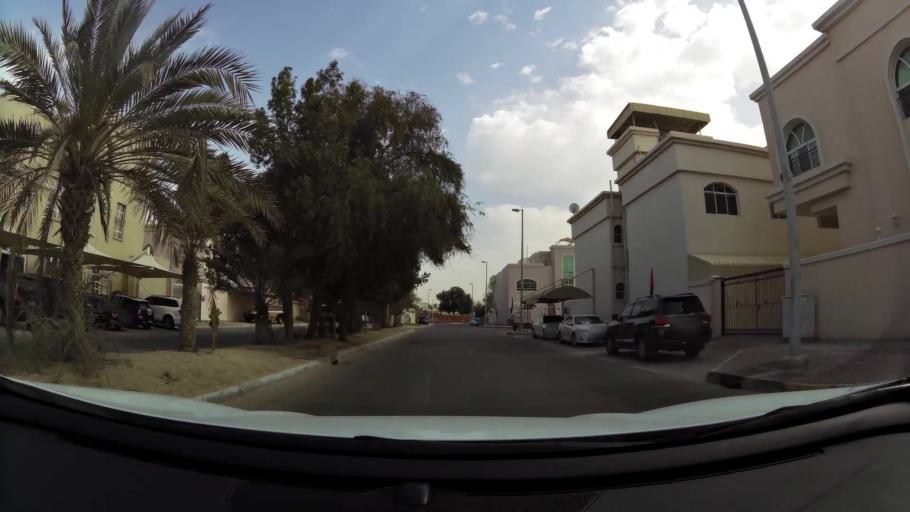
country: AE
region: Abu Dhabi
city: Abu Dhabi
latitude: 24.4432
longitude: 54.3661
